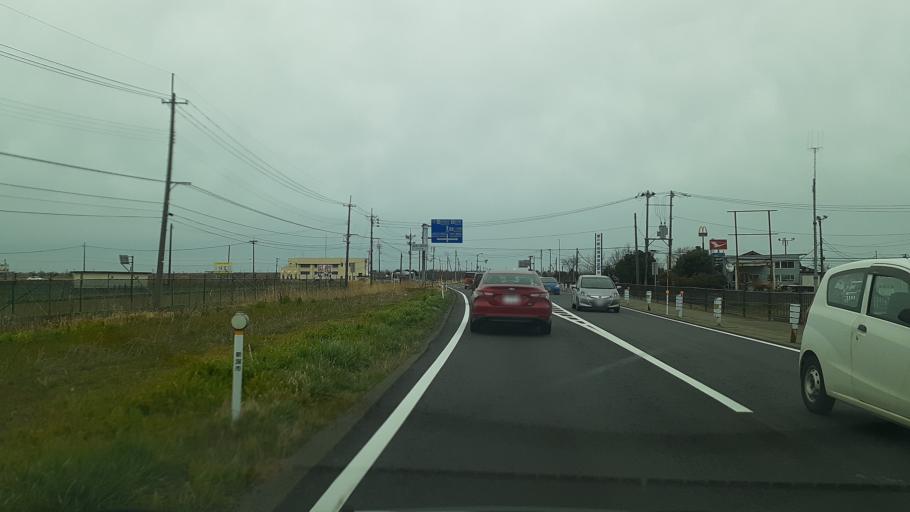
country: JP
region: Niigata
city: Niitsu-honcho
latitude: 37.8139
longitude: 139.1003
